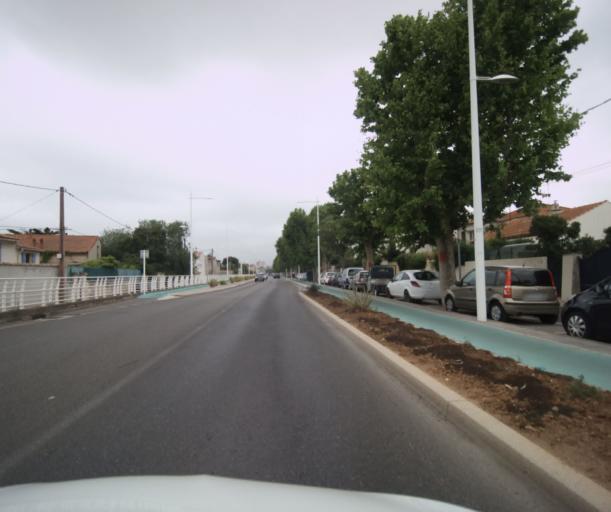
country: FR
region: Provence-Alpes-Cote d'Azur
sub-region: Departement du Var
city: Toulon
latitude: 43.1366
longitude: 5.9075
